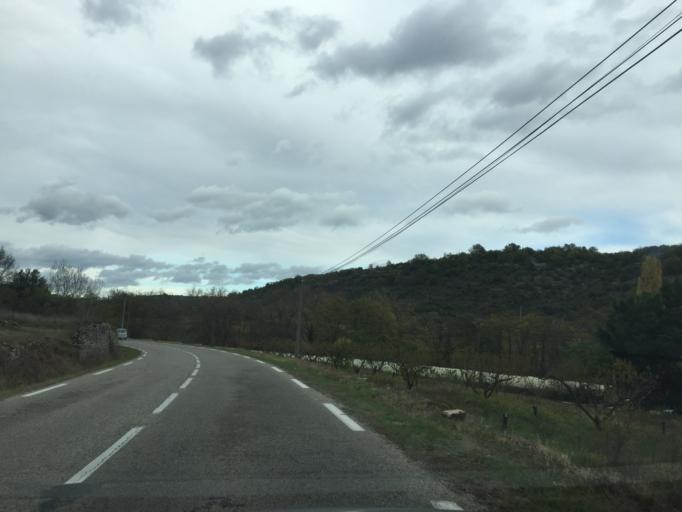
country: FR
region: Rhone-Alpes
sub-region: Departement de l'Ardeche
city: Les Vans
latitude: 44.4256
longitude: 4.1826
